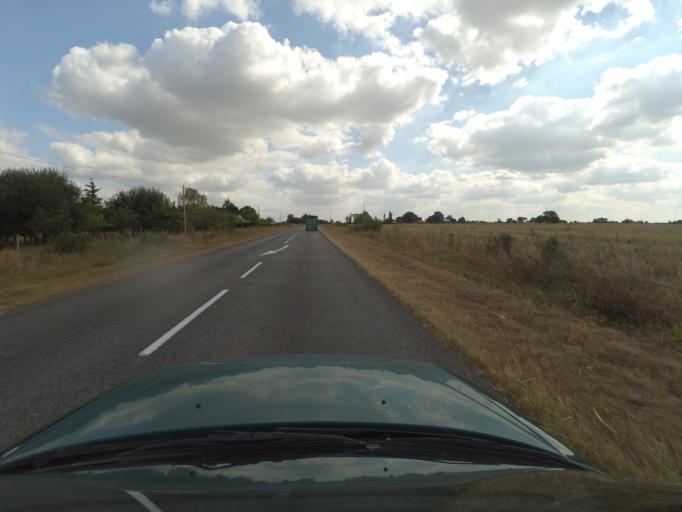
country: FR
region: Pays de la Loire
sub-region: Departement de la Loire-Atlantique
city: La Planche
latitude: 47.0468
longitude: -1.4154
